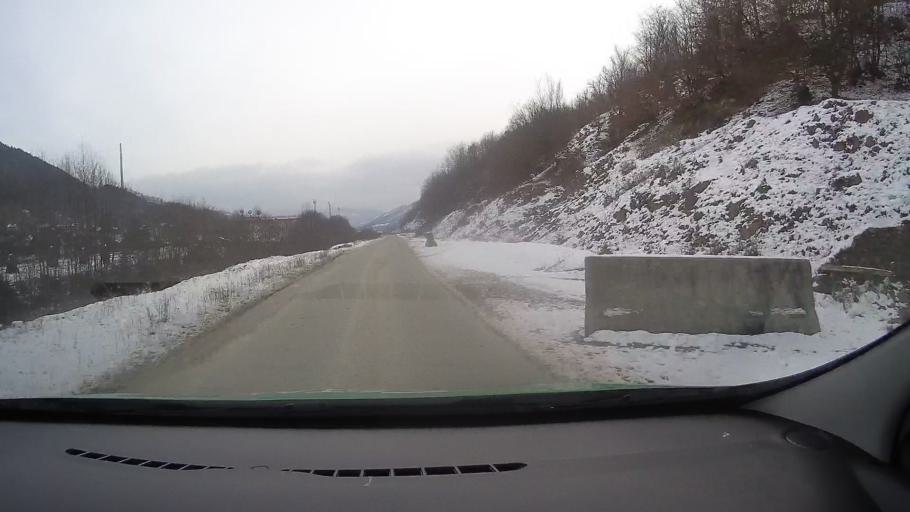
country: RO
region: Alba
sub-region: Oras Zlatna
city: Zlatna
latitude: 46.1166
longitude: 23.2072
